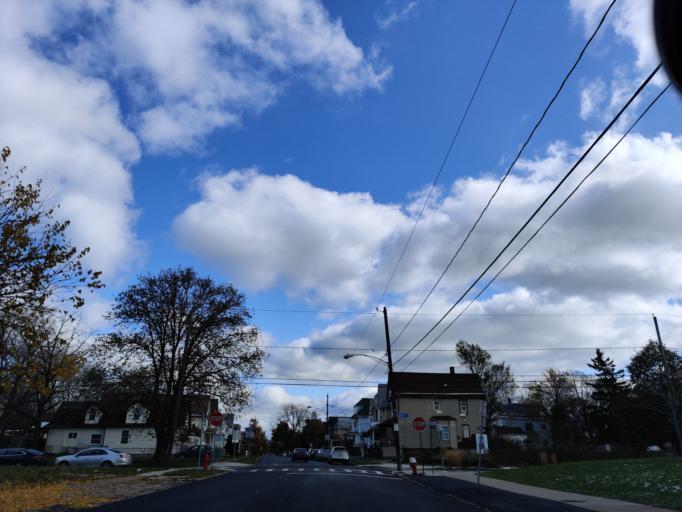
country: US
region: New York
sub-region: Erie County
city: Buffalo
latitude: 42.9220
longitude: -78.8957
